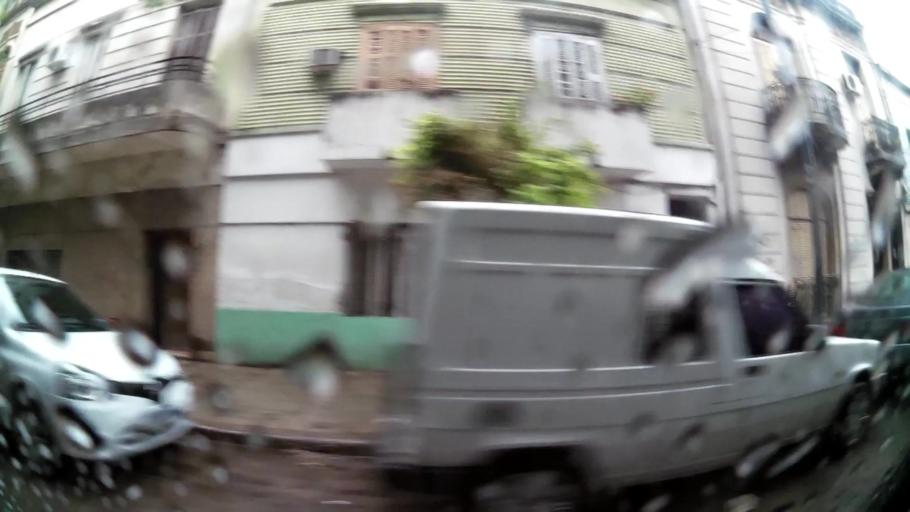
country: AR
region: Buenos Aires
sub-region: Partido de Avellaneda
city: Avellaneda
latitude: -34.6352
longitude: -58.3626
